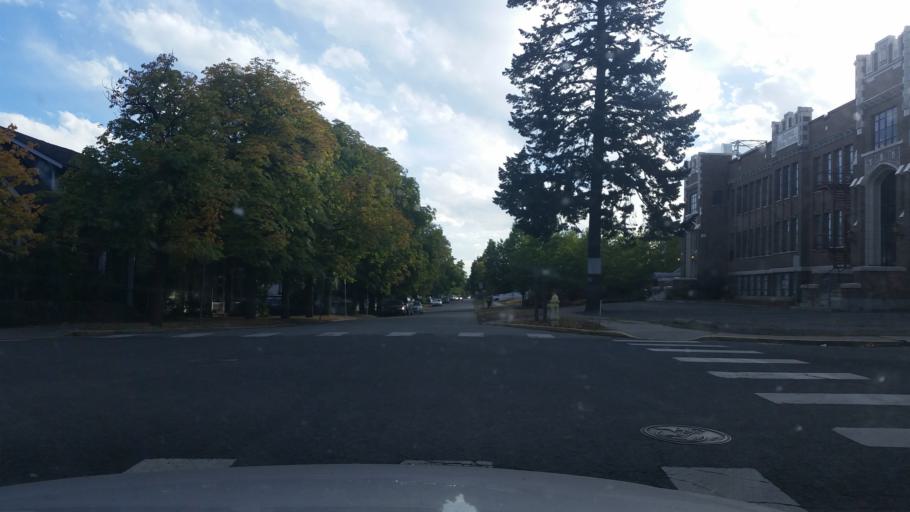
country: US
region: Washington
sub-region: Spokane County
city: Cheney
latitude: 47.4898
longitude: -117.5768
